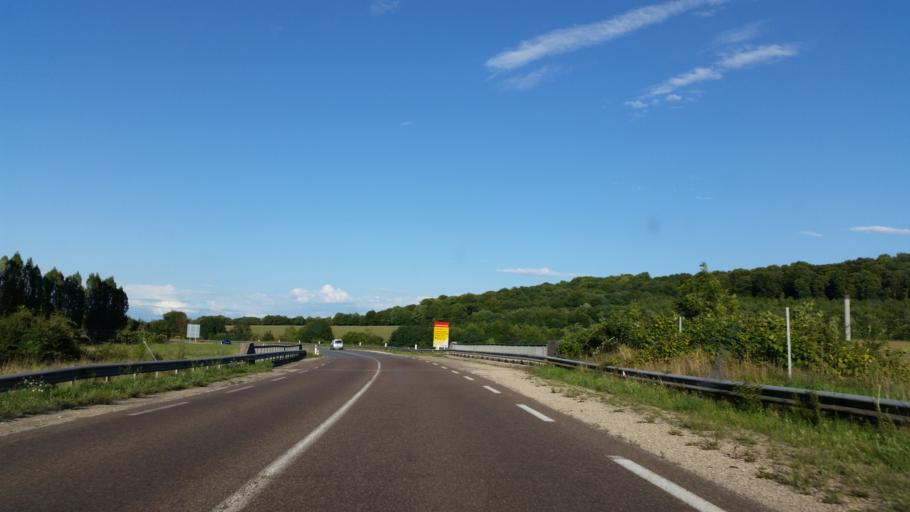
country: FR
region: Franche-Comte
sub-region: Departement de la Haute-Saone
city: Hericourt
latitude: 47.5908
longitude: 6.7947
